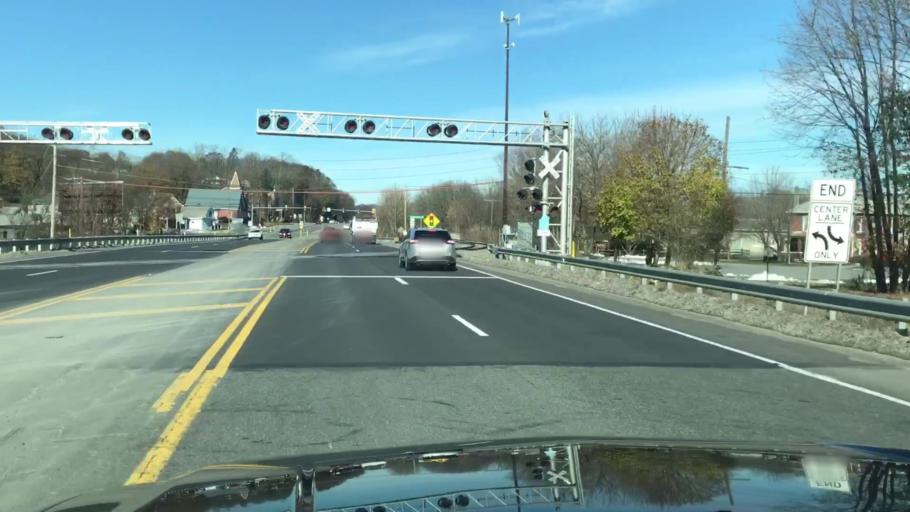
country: US
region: Pennsylvania
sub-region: Northumberland County
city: Northumberland
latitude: 40.9097
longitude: -76.8529
